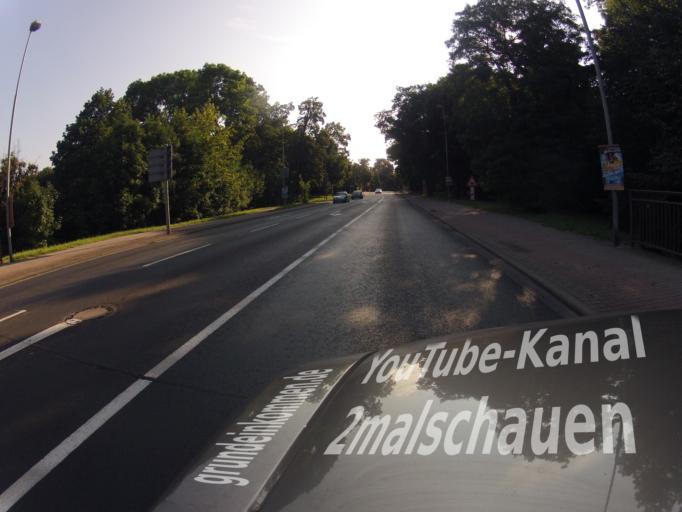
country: DE
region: Saxony
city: Torgau
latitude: 51.5569
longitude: 12.9932
